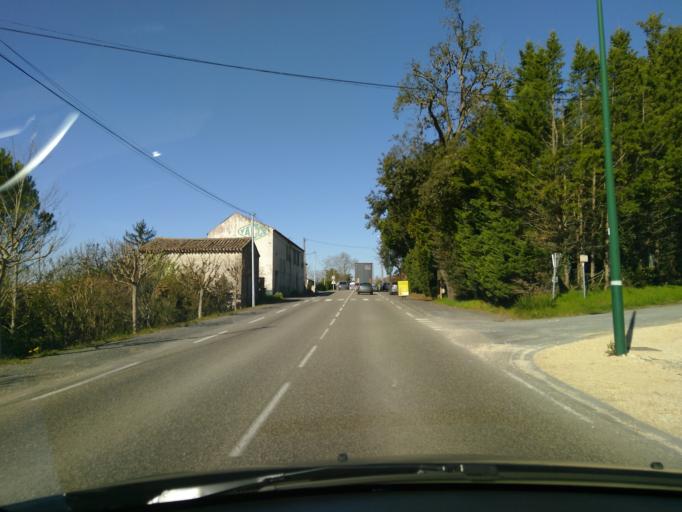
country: FR
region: Aquitaine
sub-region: Departement du Lot-et-Garonne
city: Cancon
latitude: 44.5844
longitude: 0.6230
